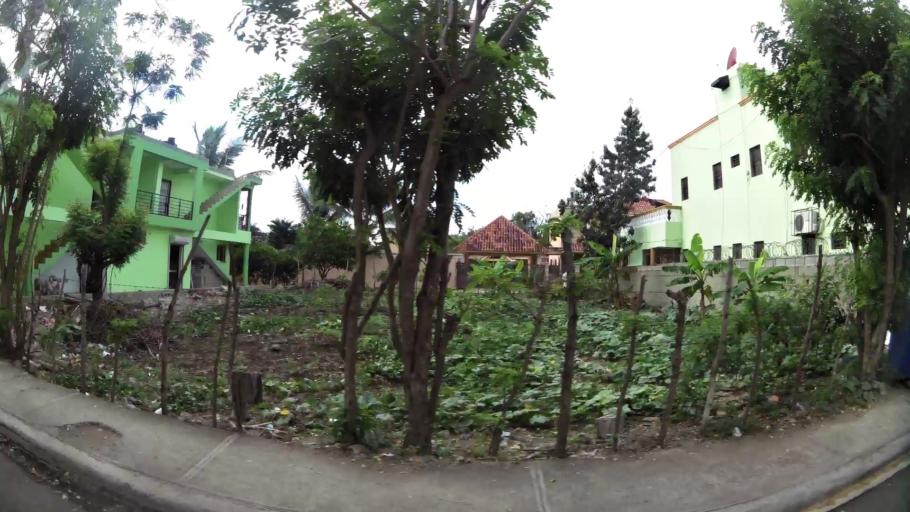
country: DO
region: Santiago
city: Santiago de los Caballeros
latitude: 19.4275
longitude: -70.6750
